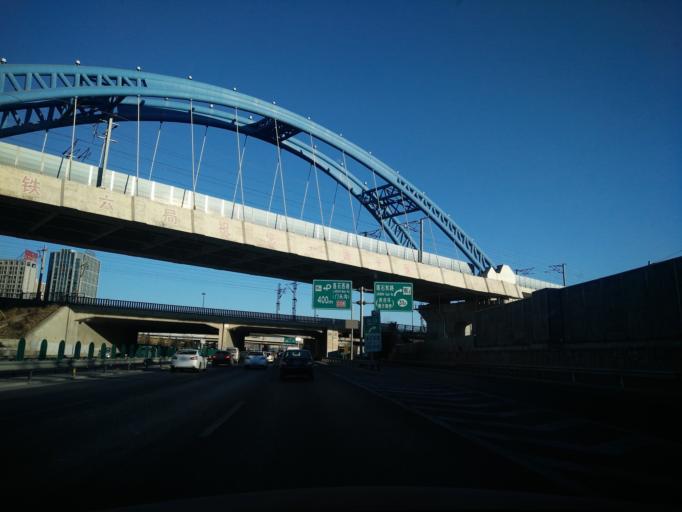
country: CN
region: Beijing
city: Lugu
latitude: 39.8902
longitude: 116.2054
